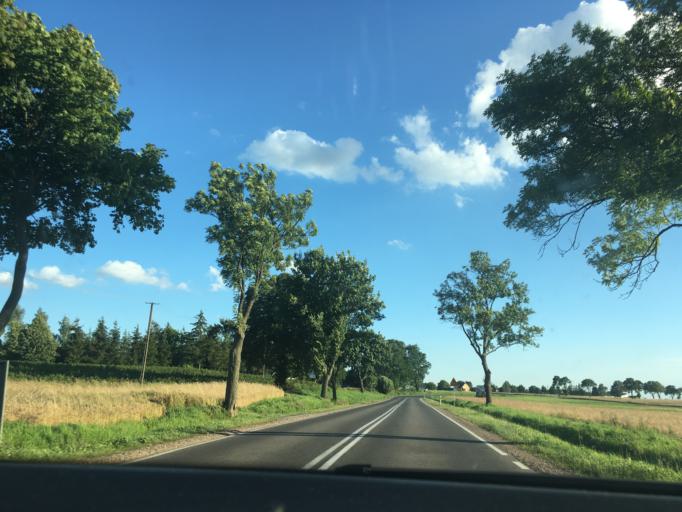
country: PL
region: Masovian Voivodeship
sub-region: Powiat losicki
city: Losice
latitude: 52.2405
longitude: 22.7743
